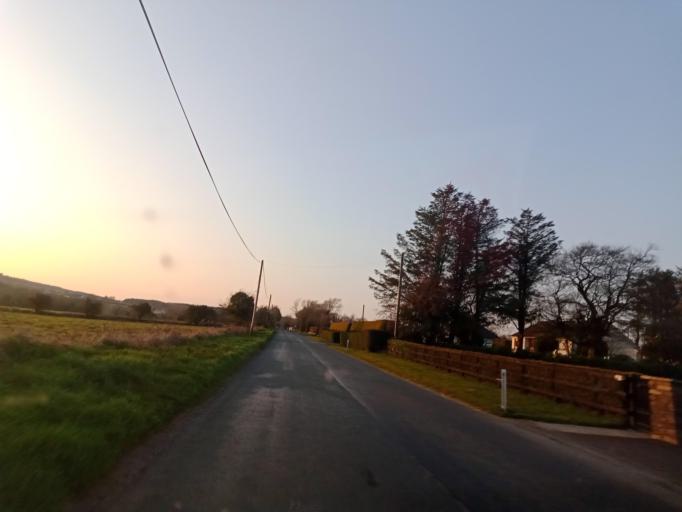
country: IE
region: Leinster
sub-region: Kilkenny
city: Castlecomer
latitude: 52.8342
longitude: -7.2383
